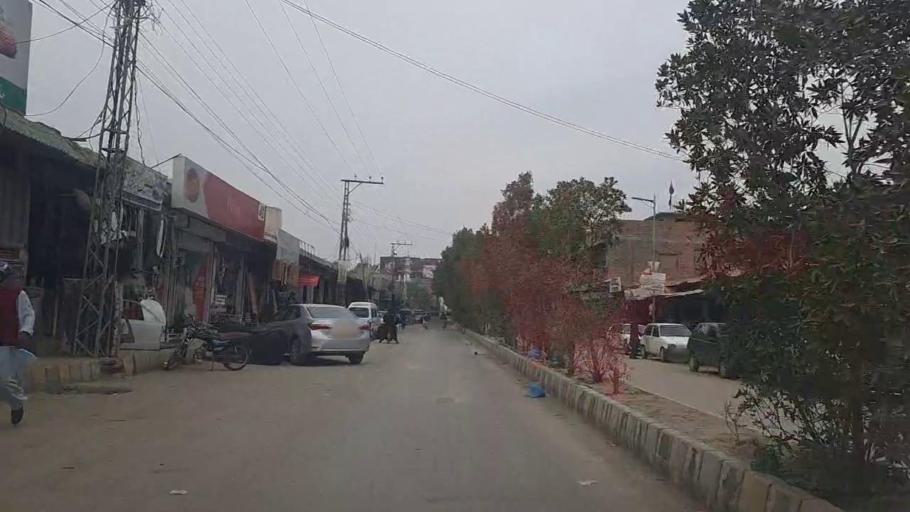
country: PK
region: Sindh
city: Nawabshah
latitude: 26.2509
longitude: 68.4052
